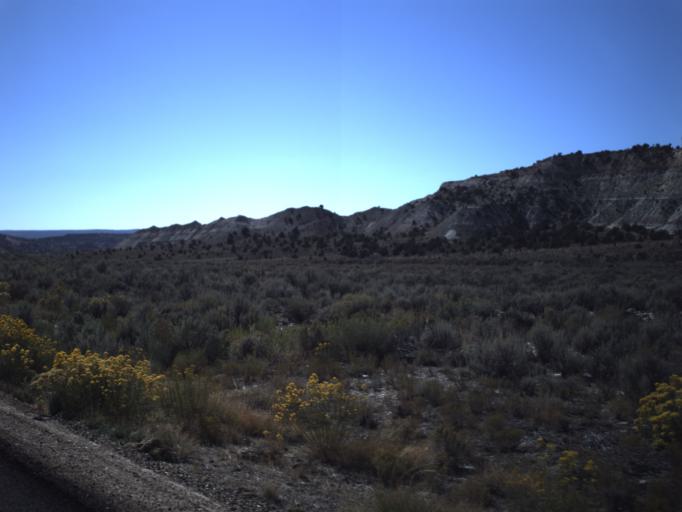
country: US
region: Utah
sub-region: Garfield County
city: Panguitch
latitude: 37.5794
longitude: -111.9858
